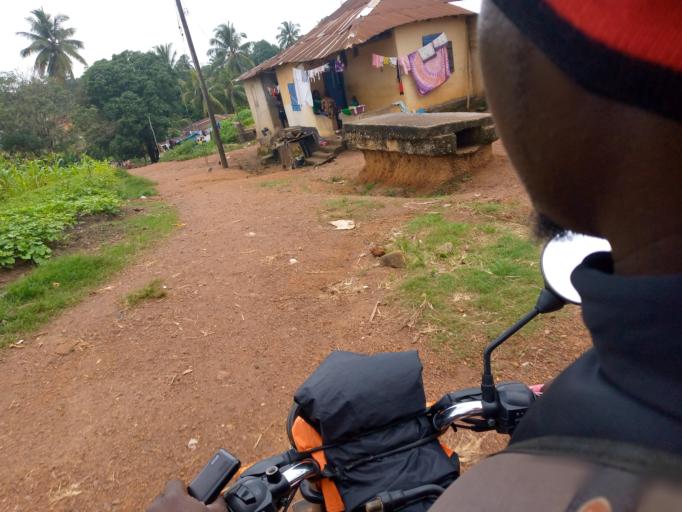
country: SL
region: Eastern Province
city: Kenema
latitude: 7.8720
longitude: -11.1850
